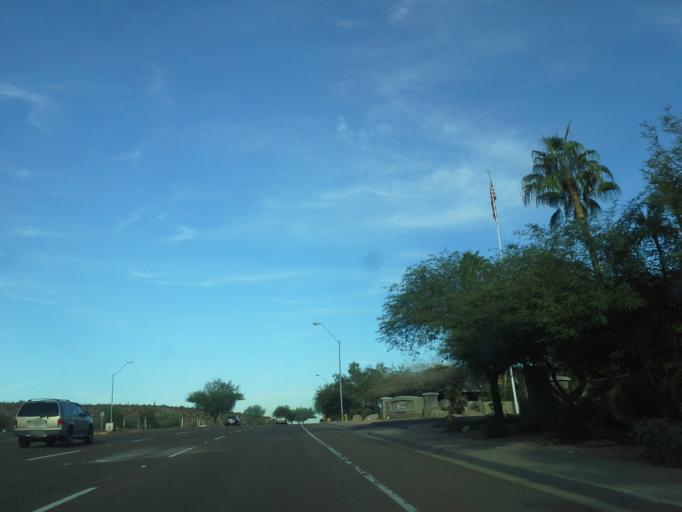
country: US
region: Arizona
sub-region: Maricopa County
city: Paradise Valley
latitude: 33.5989
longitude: -112.0449
